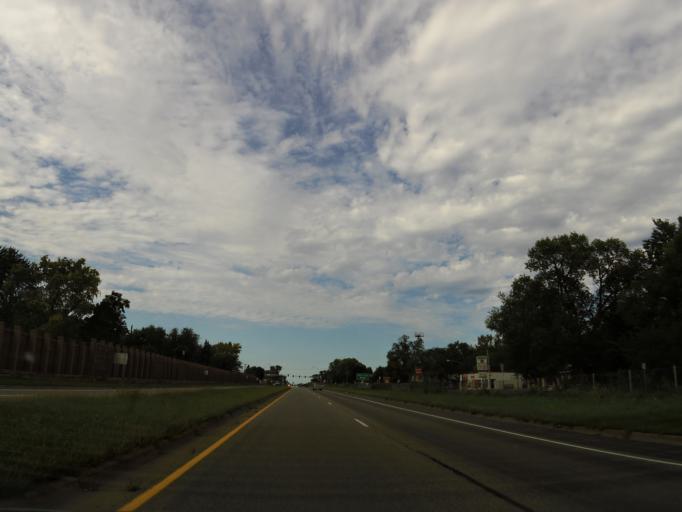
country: US
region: Minnesota
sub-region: Anoka County
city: Columbia Heights
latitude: 45.0545
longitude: -93.2631
